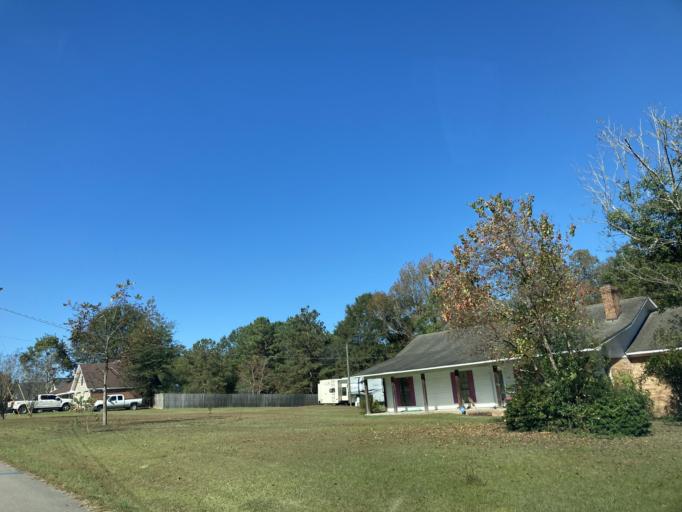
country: US
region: Mississippi
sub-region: Lamar County
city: West Hattiesburg
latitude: 31.2999
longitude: -89.4047
